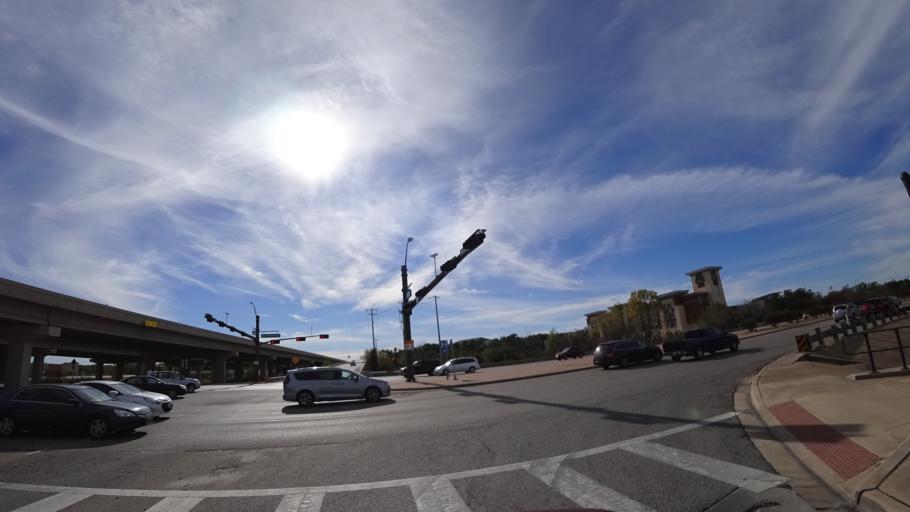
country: US
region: Texas
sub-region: Williamson County
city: Cedar Park
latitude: 30.5253
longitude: -97.8169
